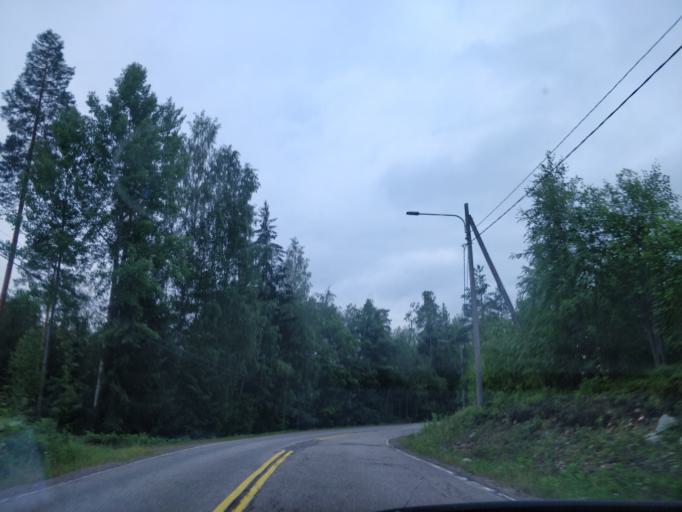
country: FI
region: Uusimaa
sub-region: Helsinki
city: Kauniainen
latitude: 60.3011
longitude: 24.6976
